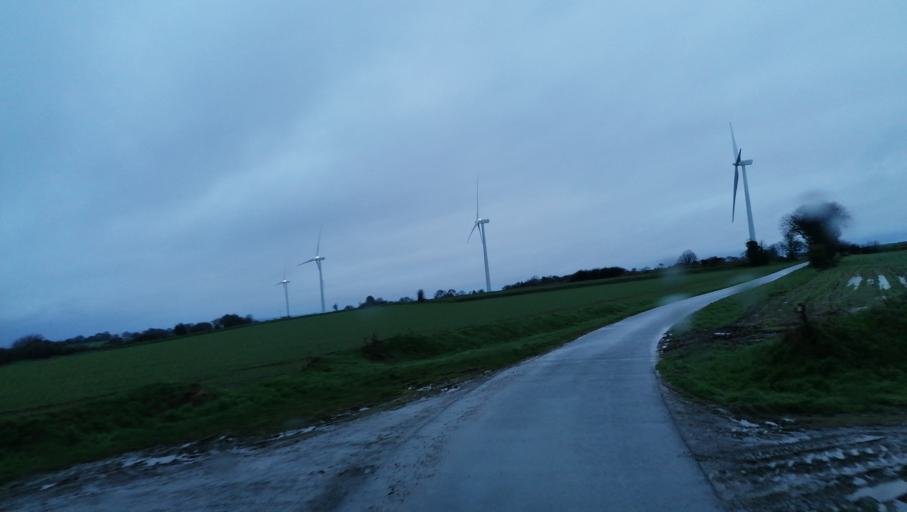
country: FR
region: Brittany
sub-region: Departement des Cotes-d'Armor
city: Lanrodec
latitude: 48.4832
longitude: -2.9989
